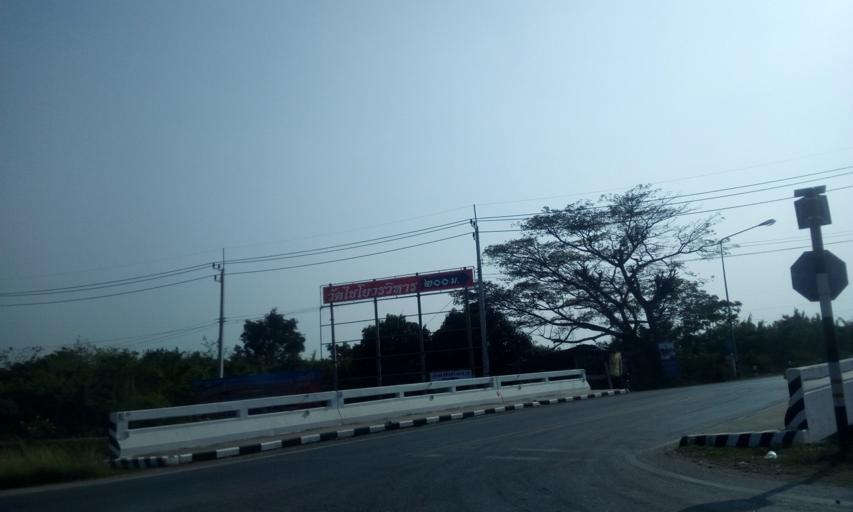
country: TH
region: Ang Thong
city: Chaiyo
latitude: 14.7149
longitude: 100.4362
